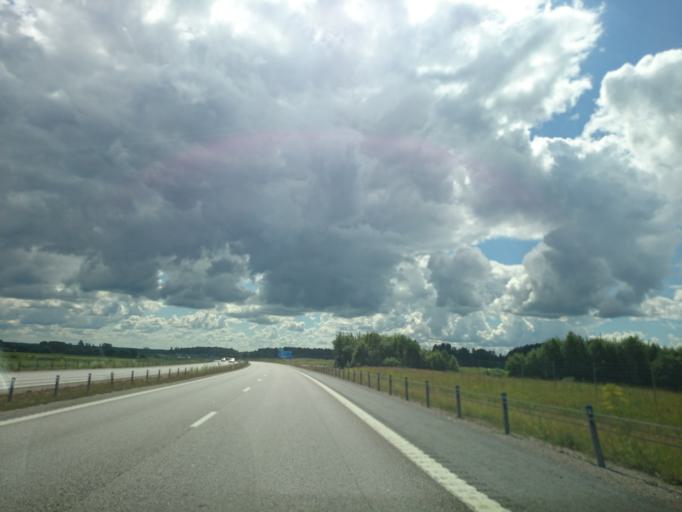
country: SE
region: Uppsala
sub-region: Tierps Kommun
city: Tierp
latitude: 60.3525
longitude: 17.4733
